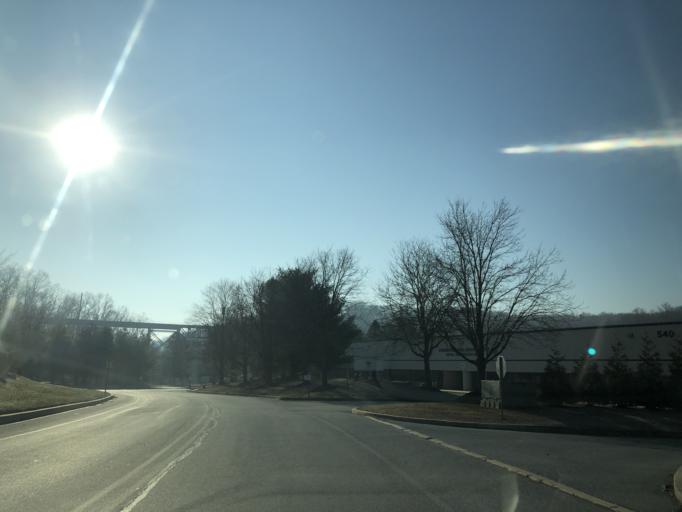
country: US
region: Pennsylvania
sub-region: Chester County
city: Downingtown
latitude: 39.9983
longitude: -75.6985
